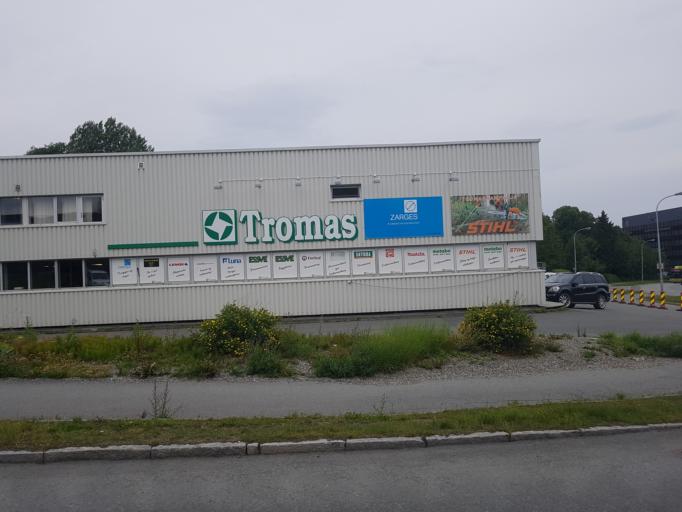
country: NO
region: Sor-Trondelag
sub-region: Trondheim
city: Trondheim
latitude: 63.3891
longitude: 10.3973
